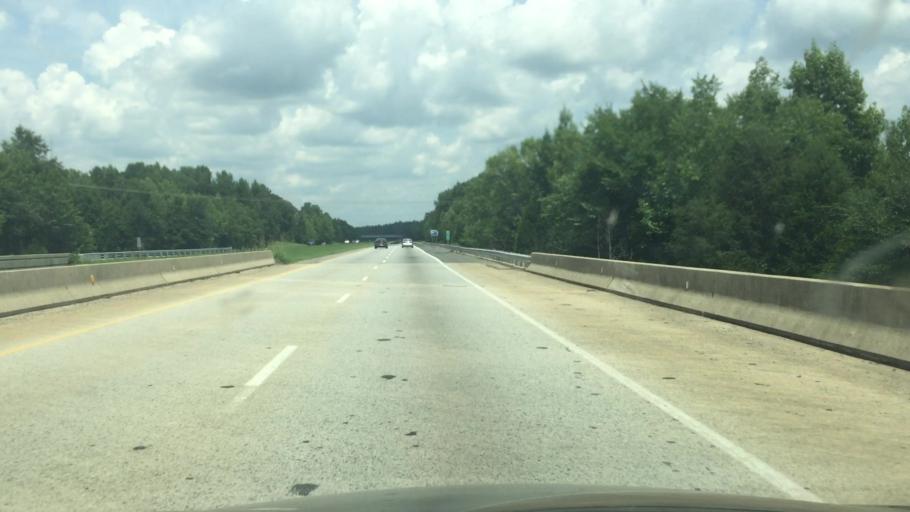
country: US
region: North Carolina
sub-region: Guilford County
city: Pleasant Garden
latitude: 35.9424
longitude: -79.8251
